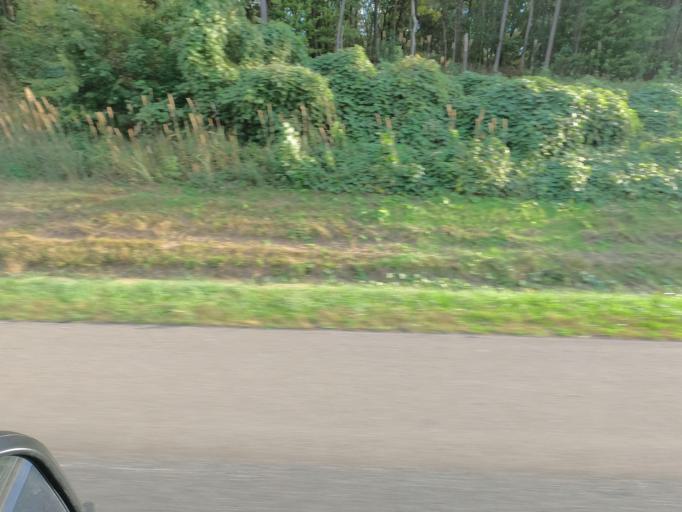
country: US
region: Tennessee
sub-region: Decatur County
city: Parsons
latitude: 35.8182
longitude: -88.1813
